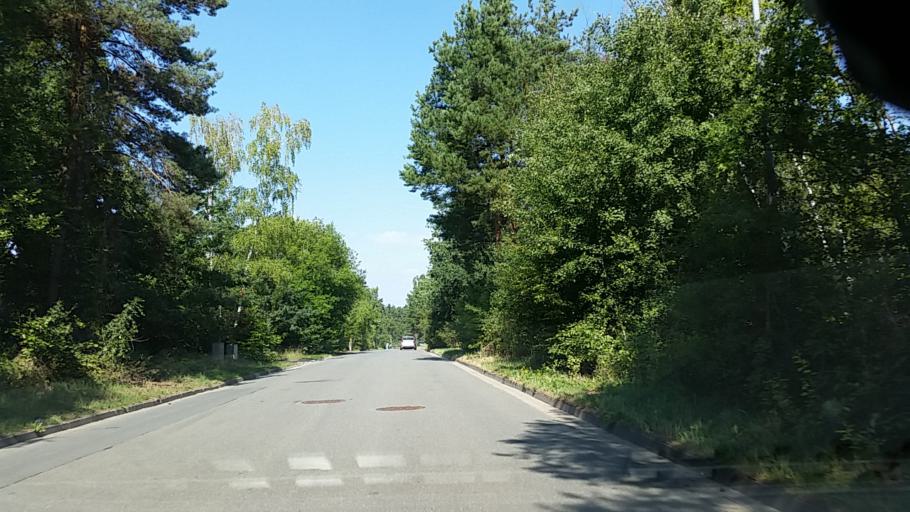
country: DE
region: Lower Saxony
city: Emmendorf
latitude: 53.0007
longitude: 10.5589
